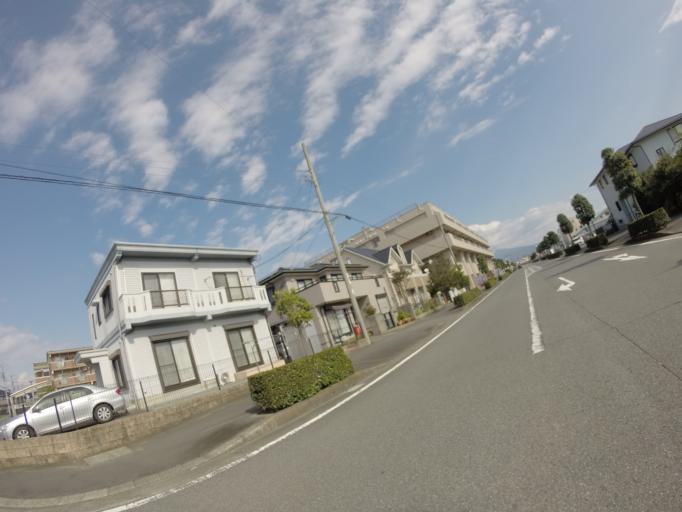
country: JP
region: Shizuoka
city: Fuji
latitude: 35.1331
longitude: 138.6634
